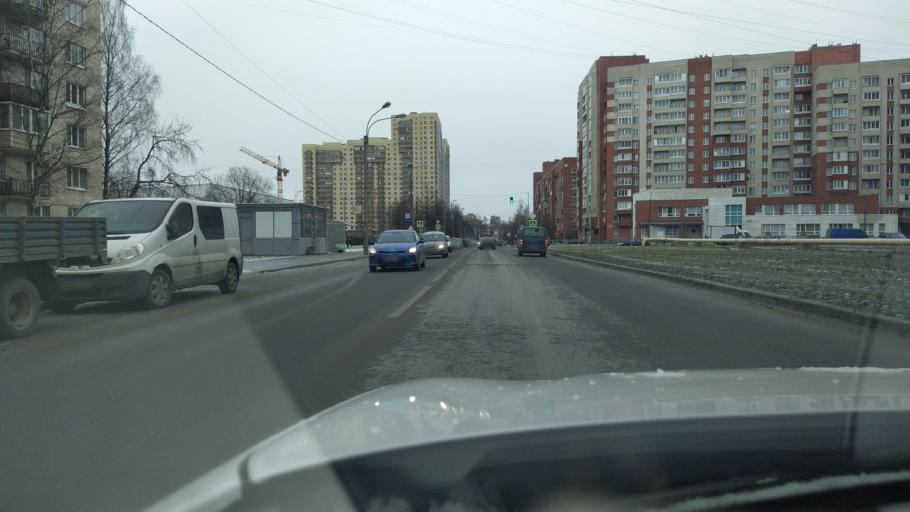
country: RU
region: Leningrad
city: Akademicheskoe
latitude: 60.0066
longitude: 30.4015
